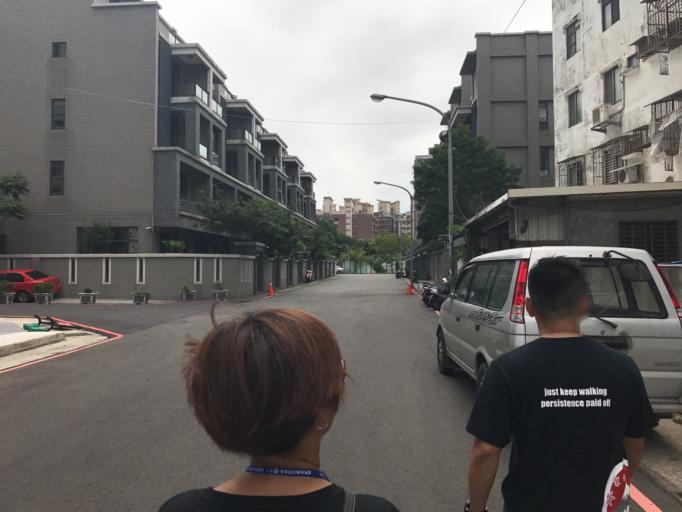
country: TW
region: Taiwan
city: Taoyuan City
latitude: 24.9441
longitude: 121.2449
